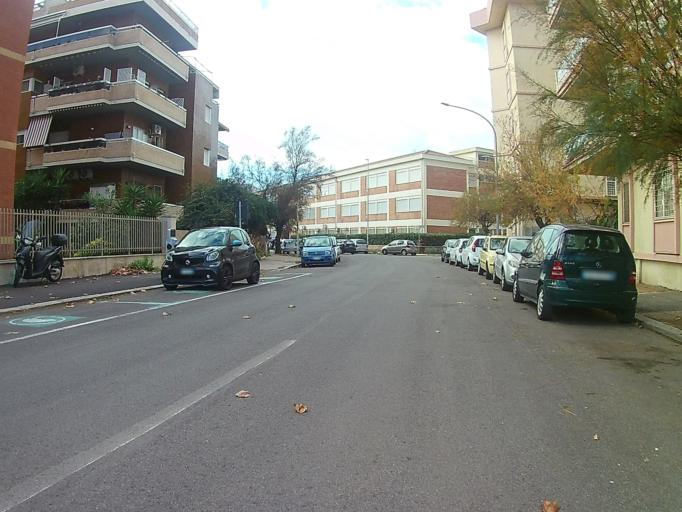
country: IT
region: Latium
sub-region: Citta metropolitana di Roma Capitale
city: Lido di Ostia
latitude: 41.7249
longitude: 12.2960
